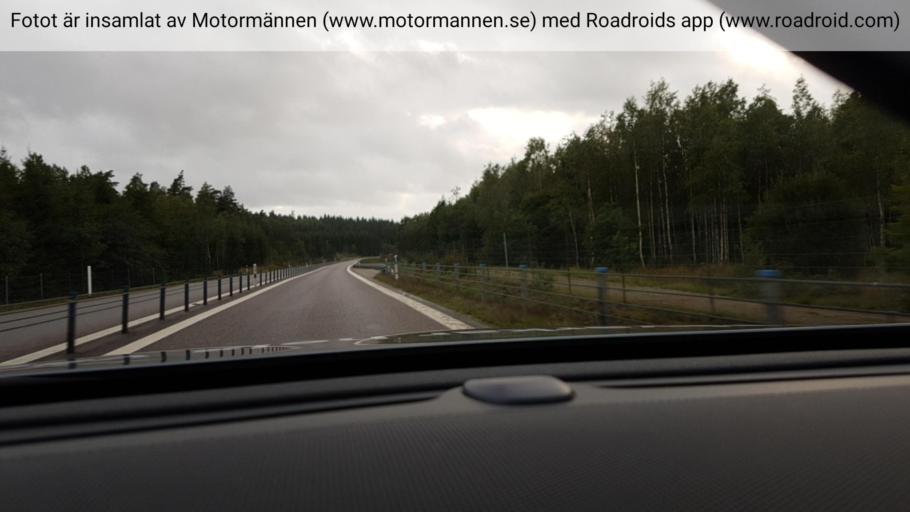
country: SE
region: Vaestra Goetaland
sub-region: Uddevalla Kommun
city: Uddevalla
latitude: 58.3284
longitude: 11.9712
